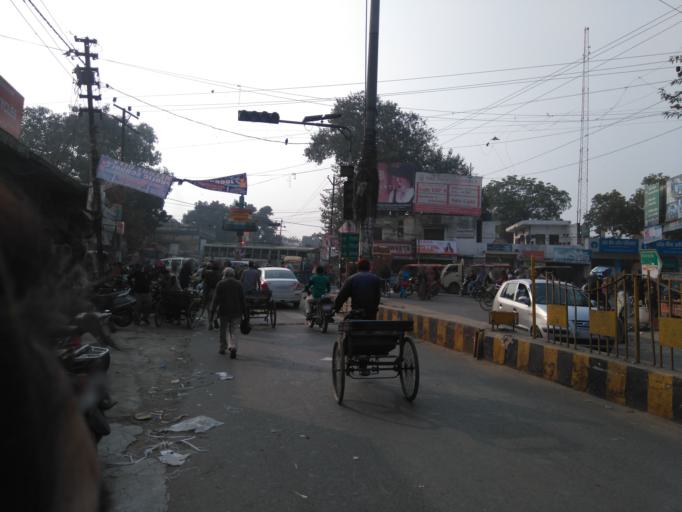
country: IN
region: Uttar Pradesh
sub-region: Meerut
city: Meerut
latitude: 28.9788
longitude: 77.6946
